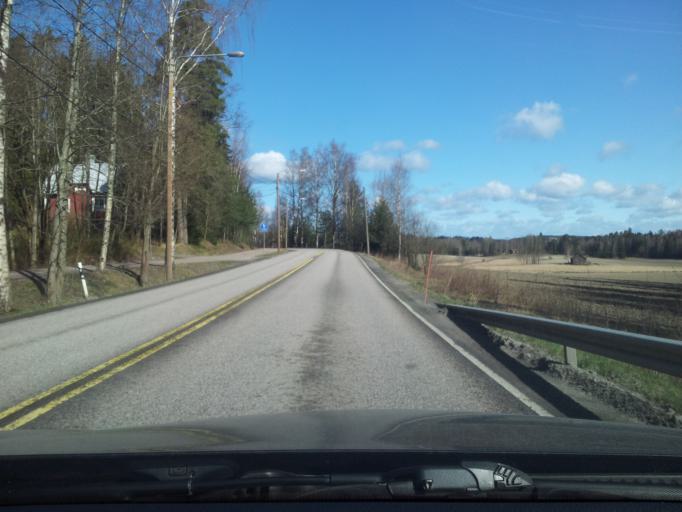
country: FI
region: Uusimaa
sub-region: Helsinki
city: Espoo
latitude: 60.1848
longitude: 24.6695
